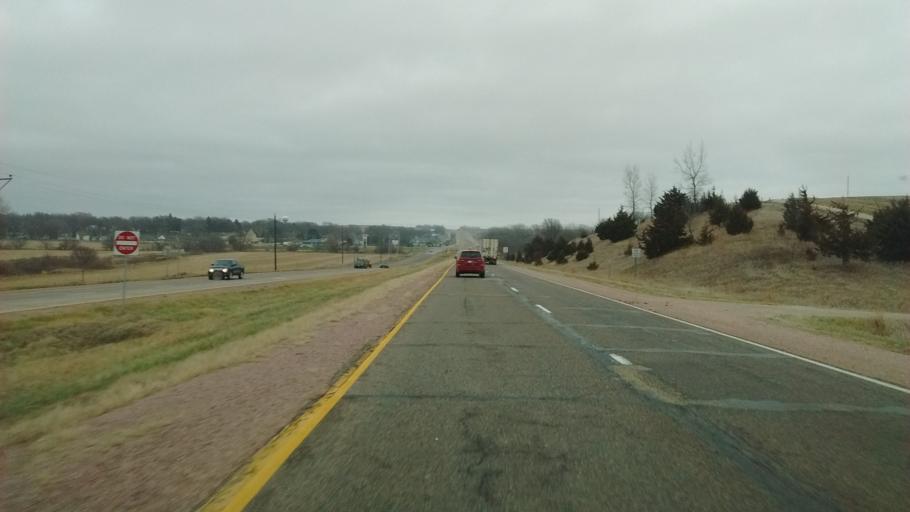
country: US
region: Iowa
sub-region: Woodbury County
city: Moville
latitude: 42.4820
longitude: -96.0851
